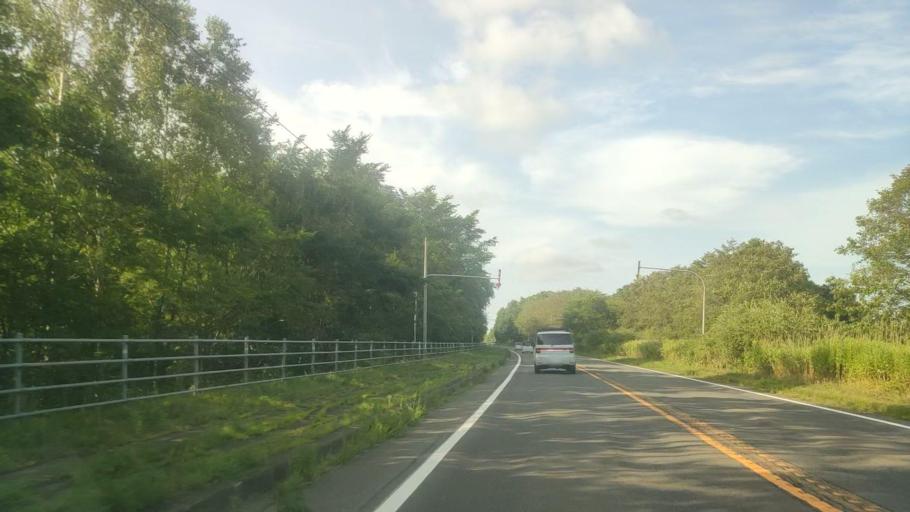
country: JP
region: Hokkaido
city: Chitose
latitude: 42.8619
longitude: 141.8224
